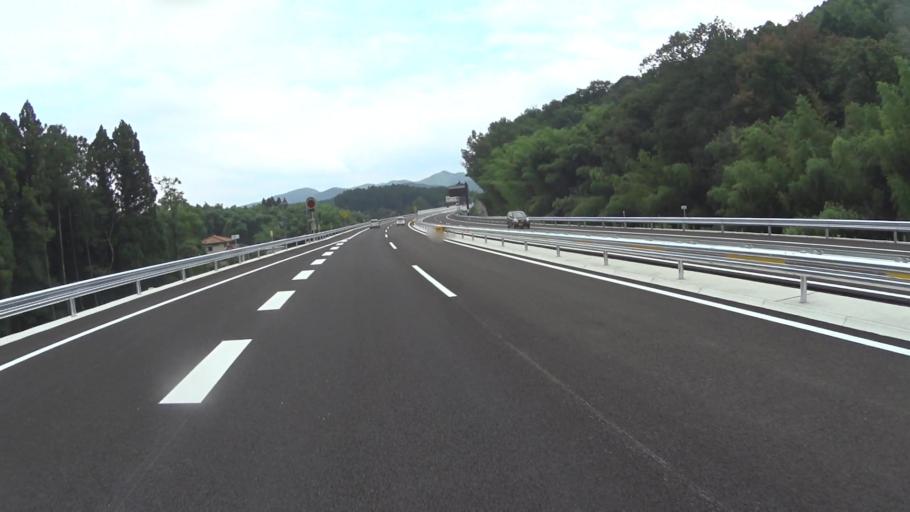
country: JP
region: Kyoto
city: Ayabe
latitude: 35.1820
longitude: 135.3666
